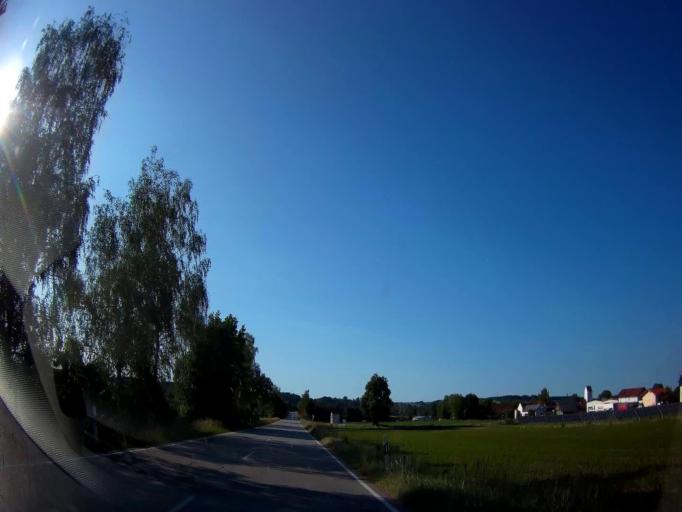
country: DE
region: Bavaria
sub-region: Lower Bavaria
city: Simbach
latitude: 48.6036
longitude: 12.7152
